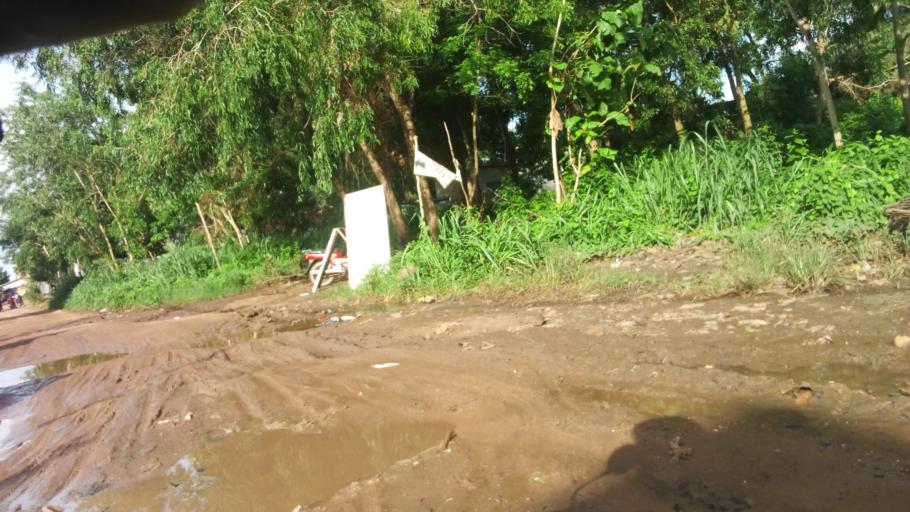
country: BJ
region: Atlantique
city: Abomey-Calavi
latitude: 6.4246
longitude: 2.3386
